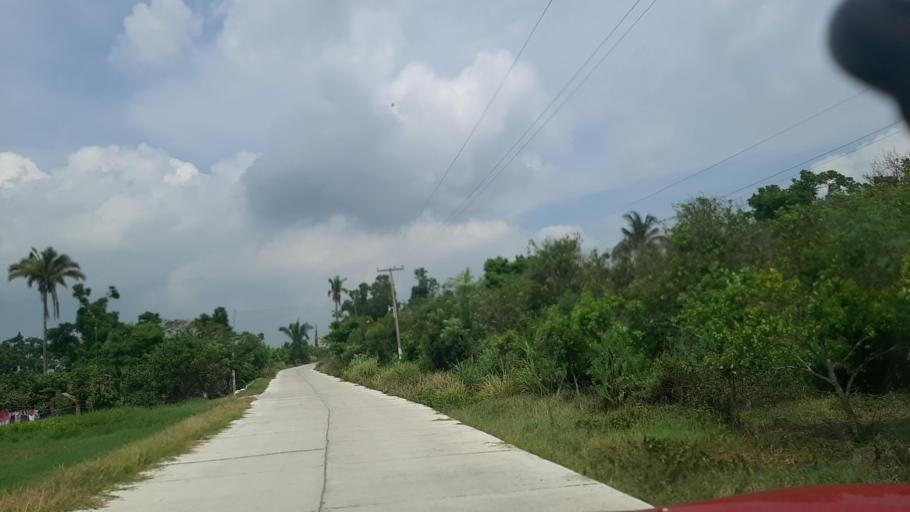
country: MX
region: Veracruz
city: Gutierrez Zamora
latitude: 20.4451
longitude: -97.1676
